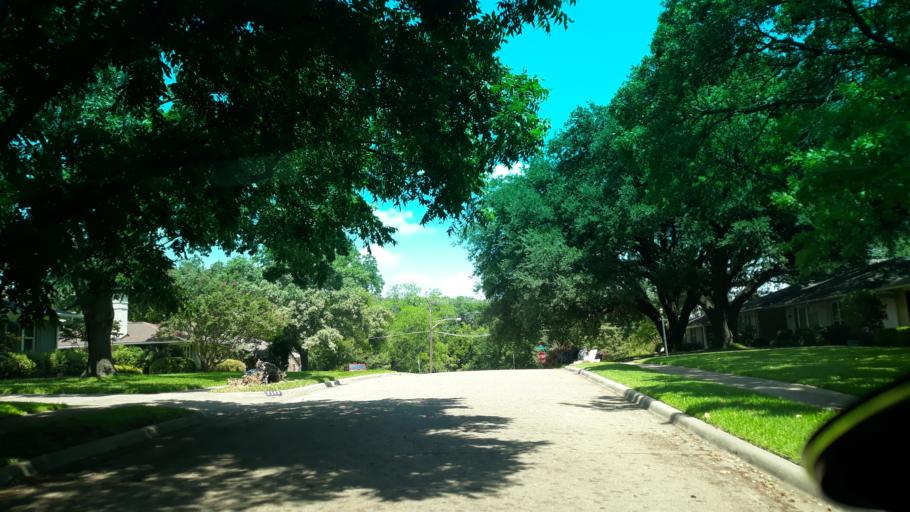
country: US
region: Texas
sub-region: Dallas County
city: Highland Park
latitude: 32.8301
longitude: -96.7360
